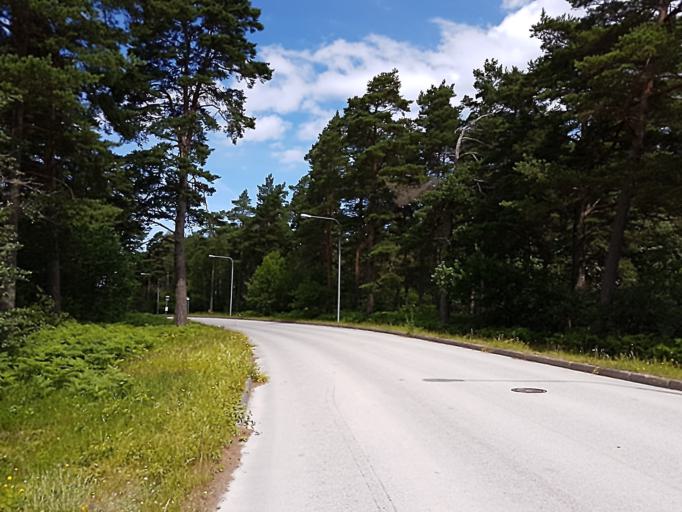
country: SE
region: Gotland
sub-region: Gotland
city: Visby
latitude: 57.6121
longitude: 18.3232
